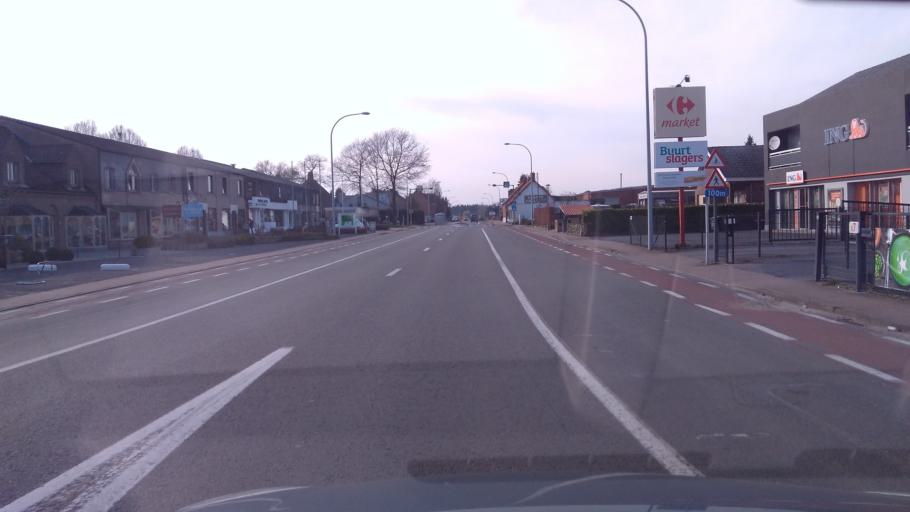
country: BE
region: Flanders
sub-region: Provincie West-Vlaanderen
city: Beernem
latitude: 51.1287
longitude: 3.3253
